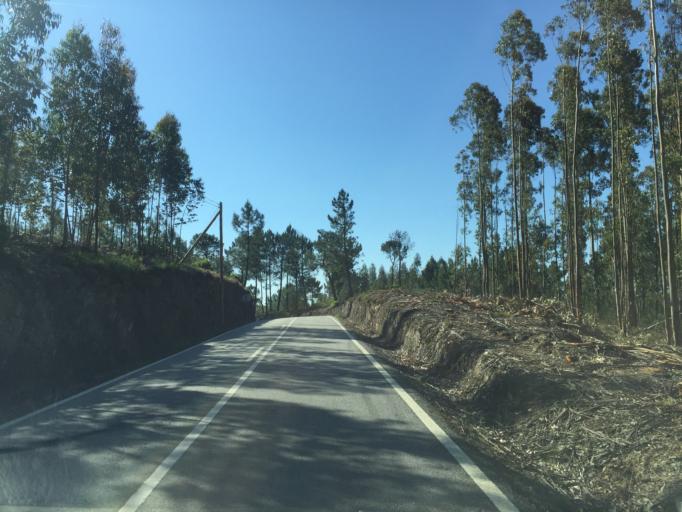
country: PT
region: Coimbra
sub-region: Pampilhosa da Serra
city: Pampilhosa da Serra
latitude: 40.0422
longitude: -7.8800
